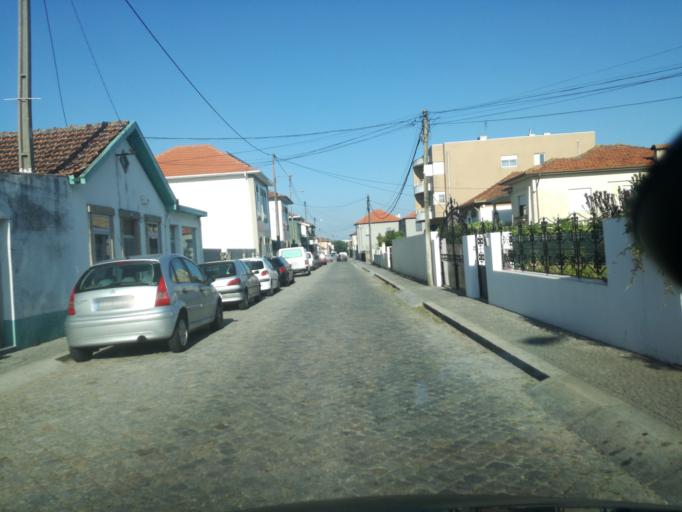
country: PT
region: Porto
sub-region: Maia
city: Gemunde
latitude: 41.2477
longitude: -8.6598
